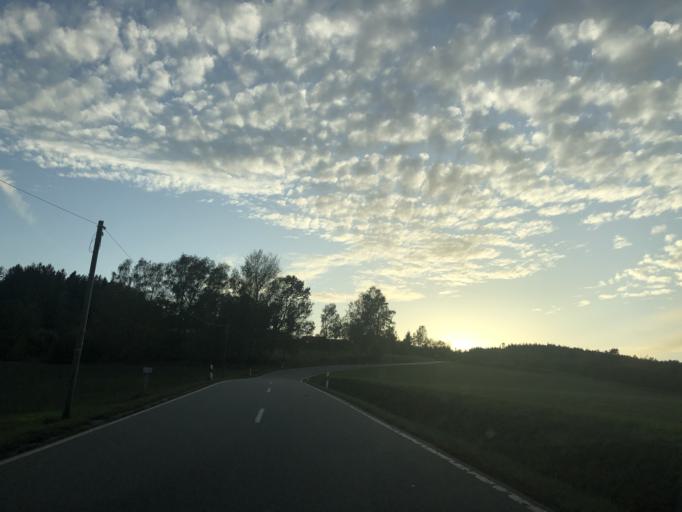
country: DE
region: Bavaria
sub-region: Lower Bavaria
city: Langdorf
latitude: 49.0162
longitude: 13.1555
